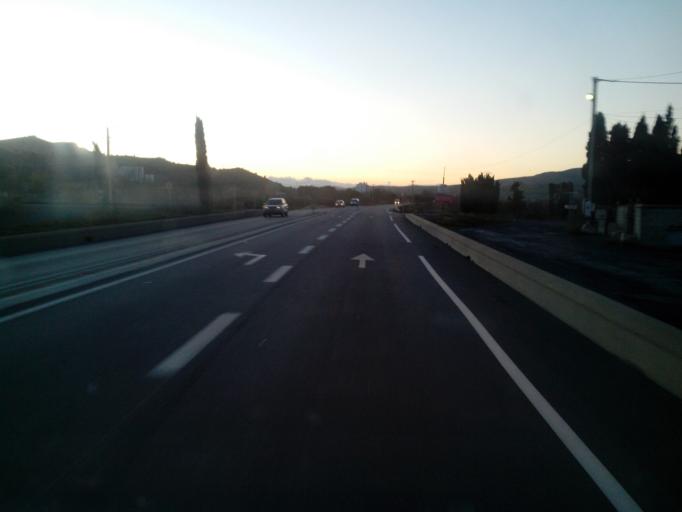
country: FR
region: Languedoc-Roussillon
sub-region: Departement des Pyrenees-Orientales
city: Baixas
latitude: 42.7788
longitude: 2.8171
